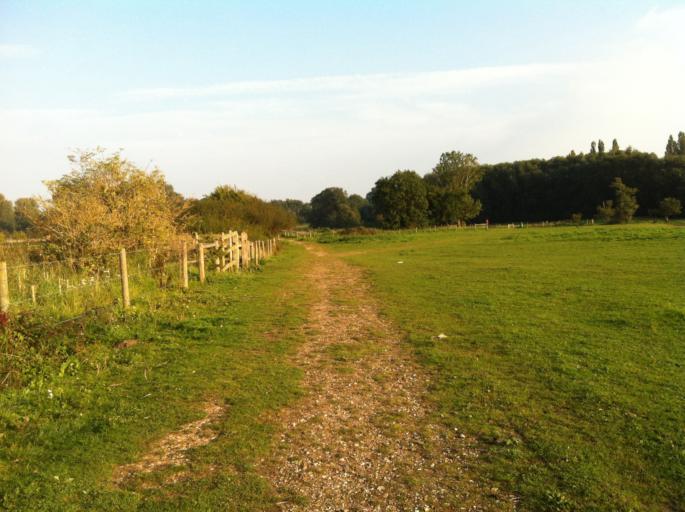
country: GB
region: England
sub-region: Norfolk
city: Bowthorpe
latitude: 52.6277
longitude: 1.2152
